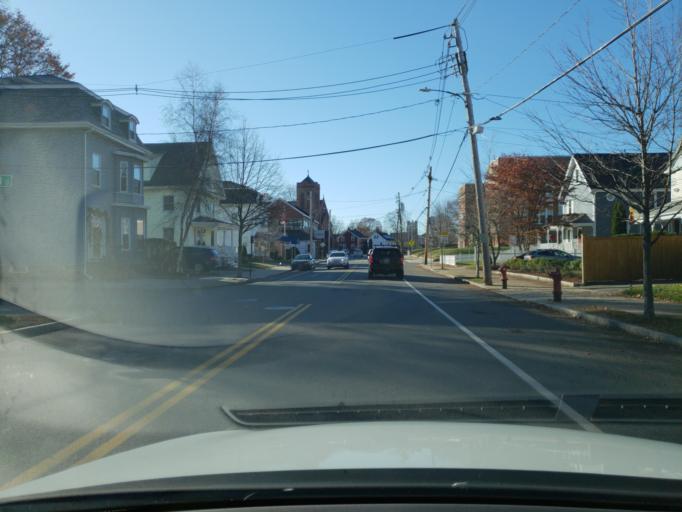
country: US
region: Massachusetts
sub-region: Middlesex County
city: Winchester
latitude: 42.4558
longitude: -71.1312
